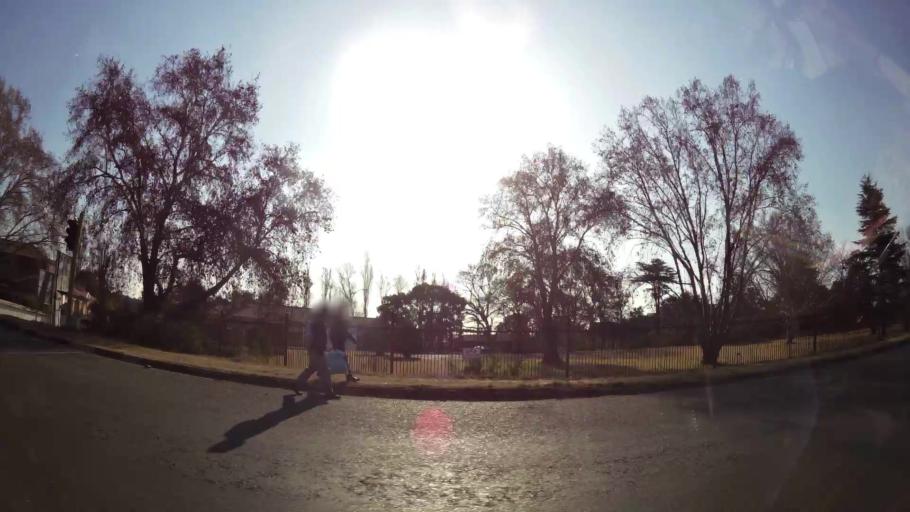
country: ZA
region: Gauteng
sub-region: West Rand District Municipality
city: Randfontein
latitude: -26.1596
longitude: 27.7154
